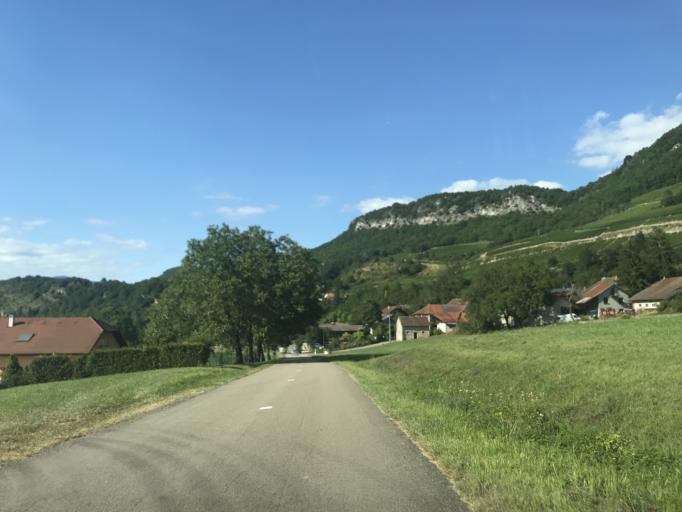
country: FR
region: Rhone-Alpes
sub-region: Departement de la Savoie
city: Yenne
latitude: 45.7422
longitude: 5.7928
